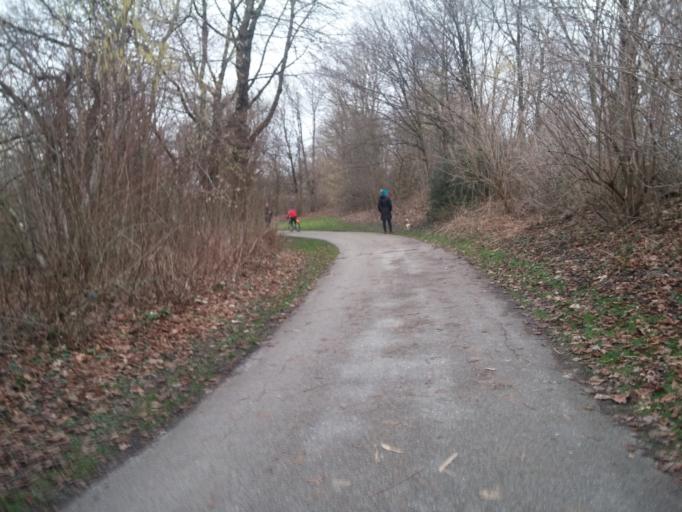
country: DE
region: Bavaria
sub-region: Upper Bavaria
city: Unterfoehring
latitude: 48.1907
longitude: 11.6712
